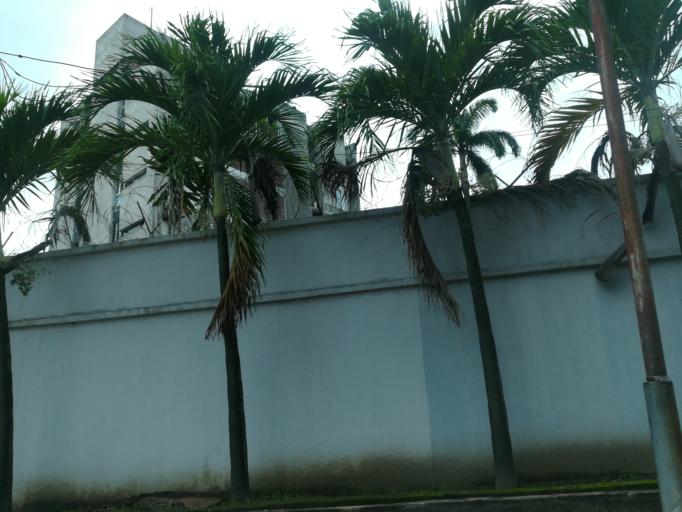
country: NG
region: Lagos
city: Lagos
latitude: 6.4339
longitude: 3.4114
